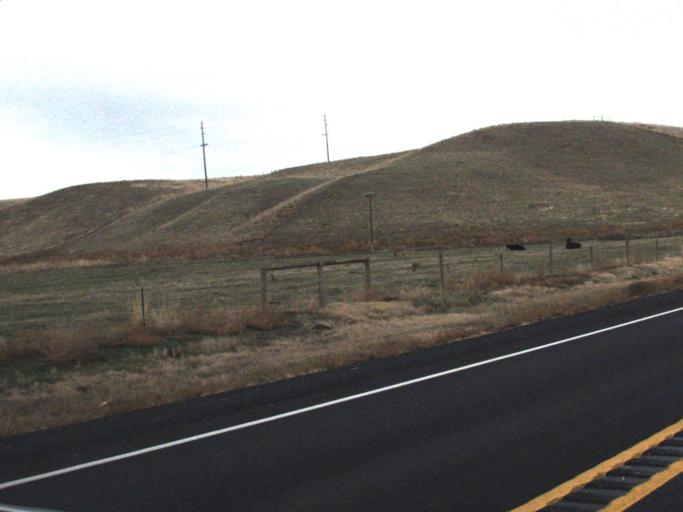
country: US
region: Washington
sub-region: Walla Walla County
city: Garrett
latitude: 46.0536
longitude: -118.6045
